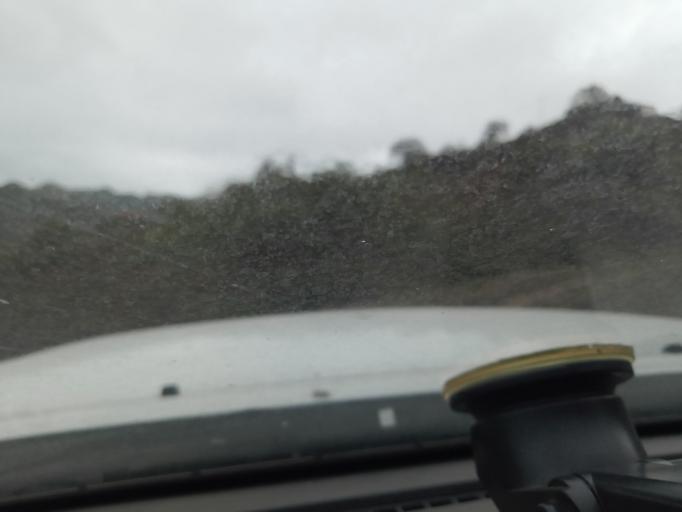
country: CV
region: Sao Salvador do Mundo
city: Picos
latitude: 15.1416
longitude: -23.6339
